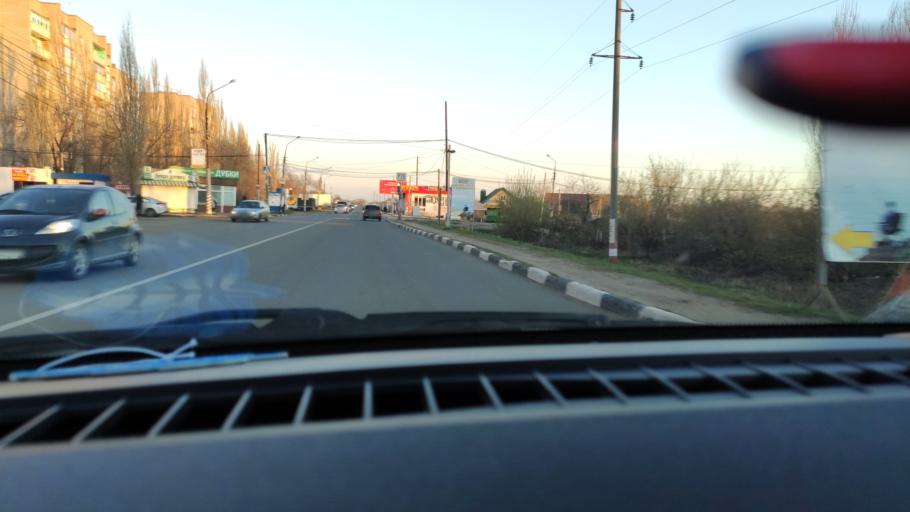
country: RU
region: Saratov
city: Privolzhskiy
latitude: 51.3898
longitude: 46.0358
